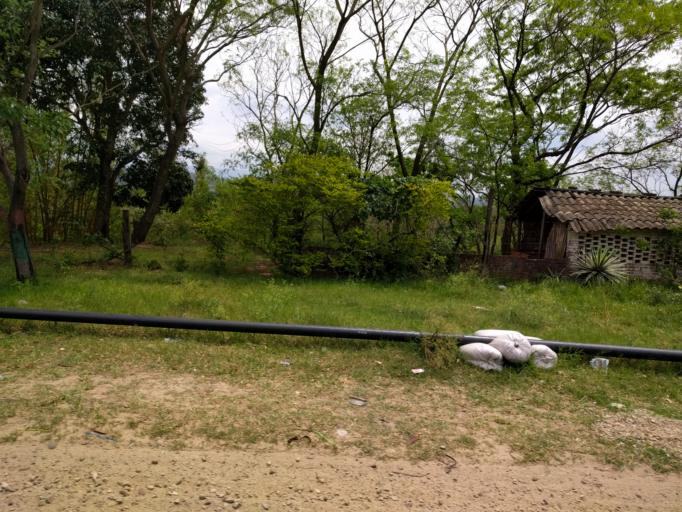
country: BO
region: Santa Cruz
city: Santa Rita
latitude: -17.9297
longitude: -63.3479
